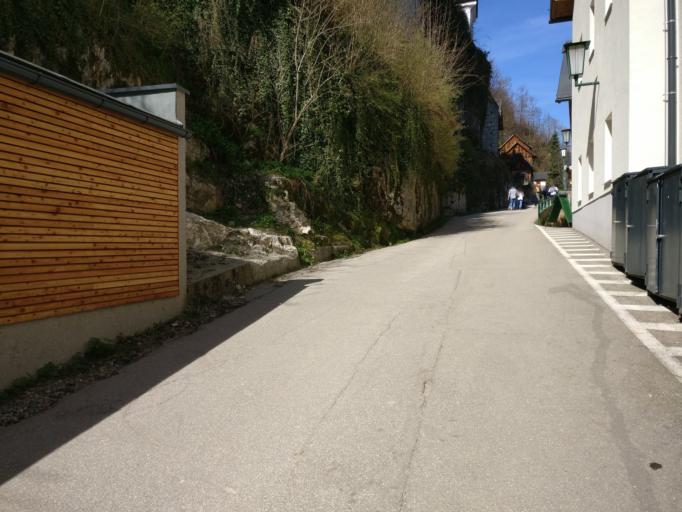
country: AT
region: Upper Austria
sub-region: Politischer Bezirk Gmunden
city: Bad Goisern
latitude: 47.5631
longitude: 13.6490
